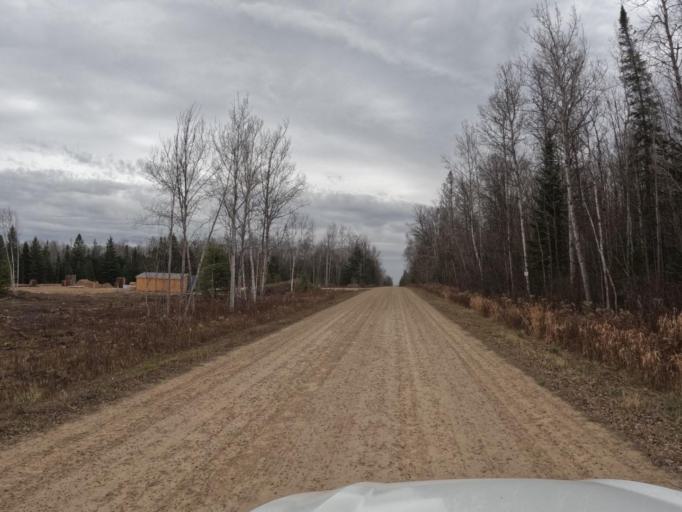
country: CA
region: Ontario
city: Shelburne
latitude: 44.0312
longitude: -80.3943
